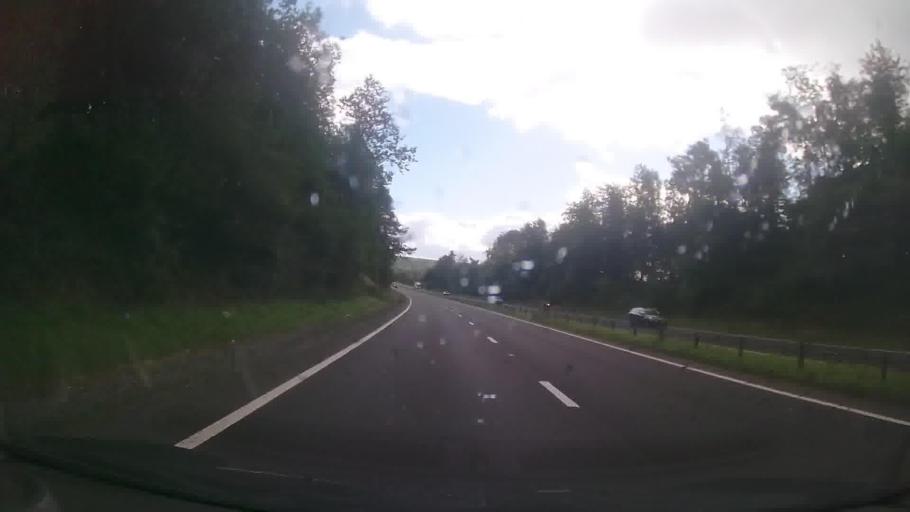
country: GB
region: Wales
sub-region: Carmarthenshire
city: Carmarthen
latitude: 51.8412
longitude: -4.2950
